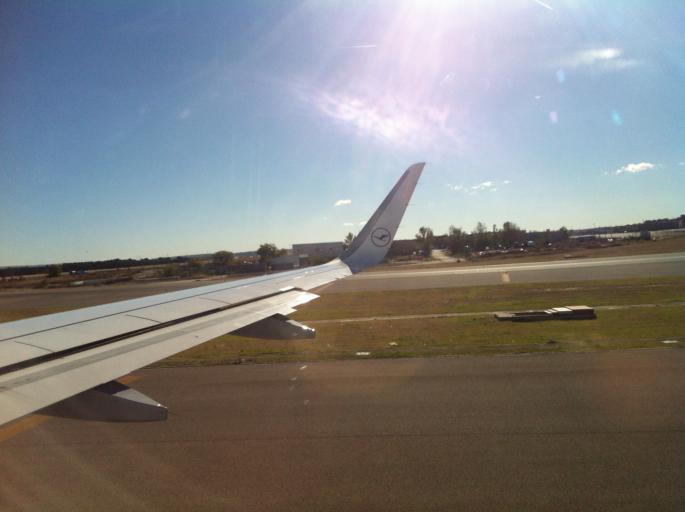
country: ES
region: Madrid
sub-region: Provincia de Madrid
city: Barajas de Madrid
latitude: 40.4886
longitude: -3.5683
